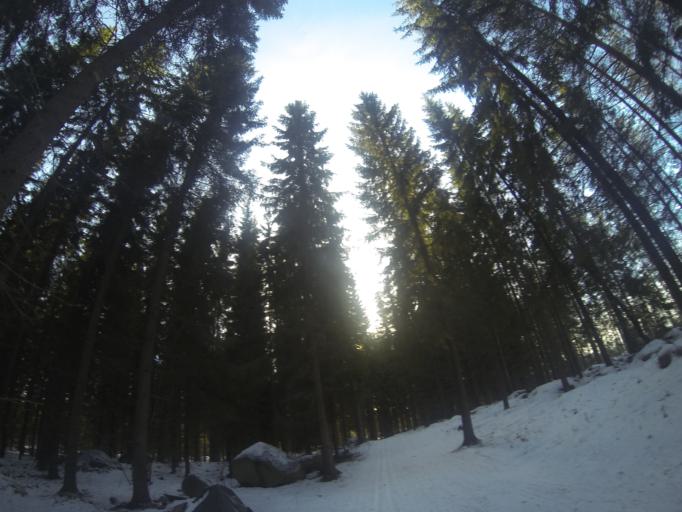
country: FI
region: Southern Savonia
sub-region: Savonlinna
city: Savonlinna
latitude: 61.9055
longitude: 28.9137
